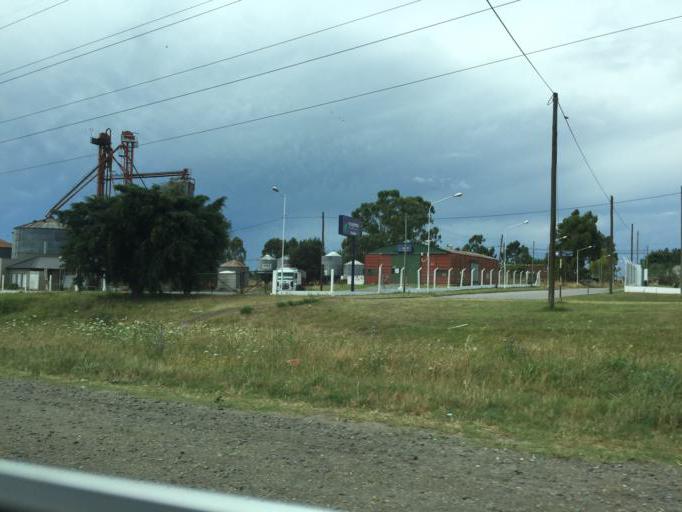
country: AR
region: Buenos Aires
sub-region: Partido de Tandil
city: Tandil
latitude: -37.3173
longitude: -59.1067
